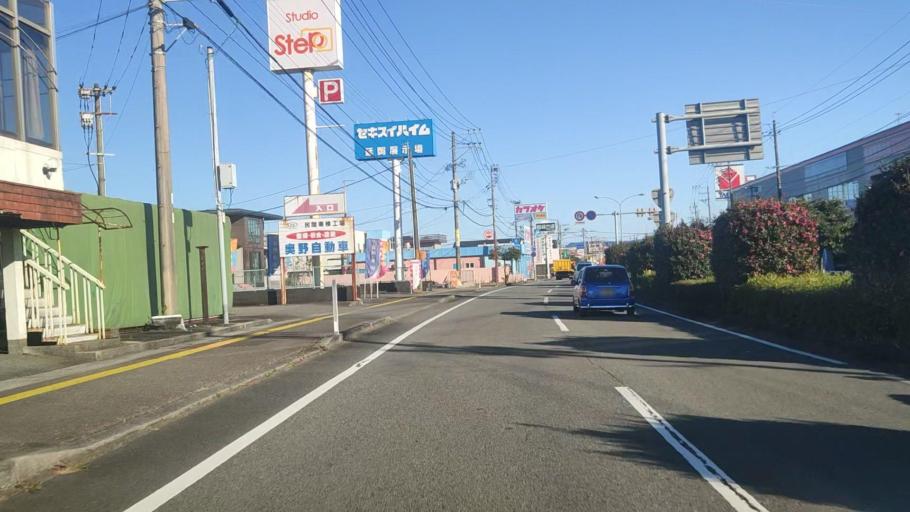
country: JP
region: Miyazaki
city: Nobeoka
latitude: 32.5496
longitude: 131.6771
